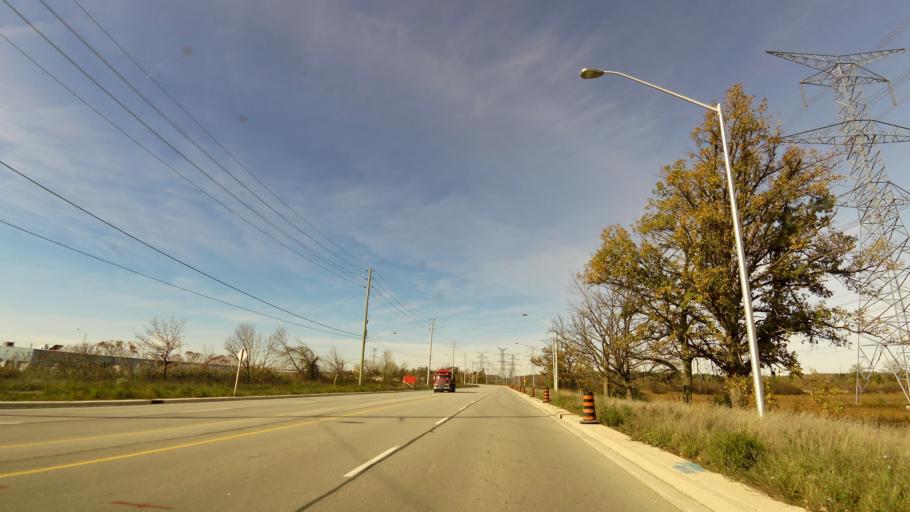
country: CA
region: Ontario
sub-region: Halton
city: Milton
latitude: 43.5458
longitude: -79.8705
